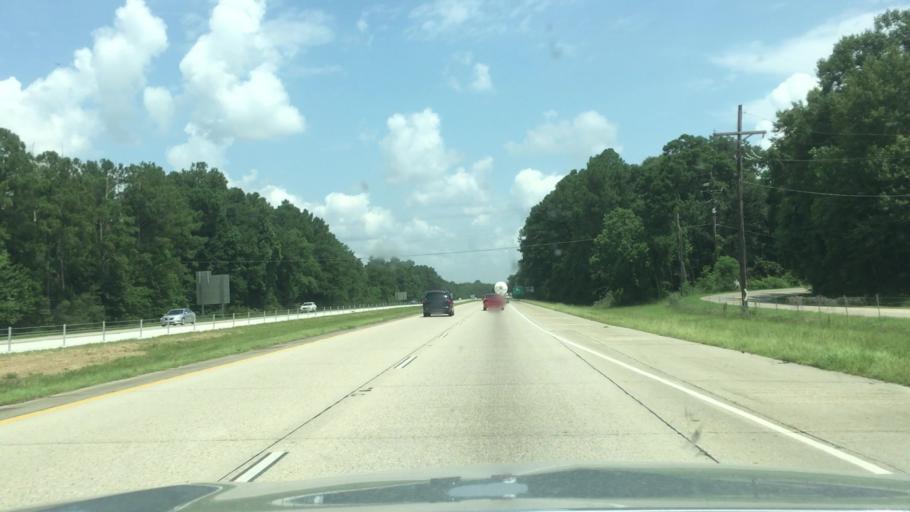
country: US
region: Louisiana
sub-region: Saint Tammany Parish
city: Pearl River
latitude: 30.3576
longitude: -89.7413
